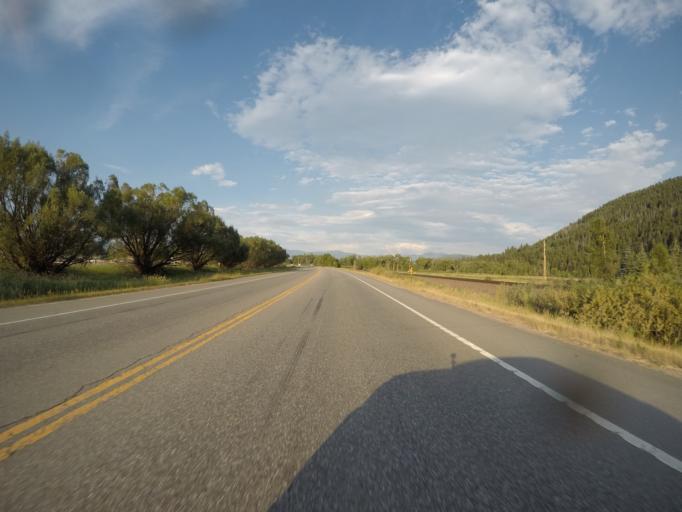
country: US
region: Colorado
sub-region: Routt County
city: Steamboat Springs
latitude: 40.4842
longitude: -106.9774
